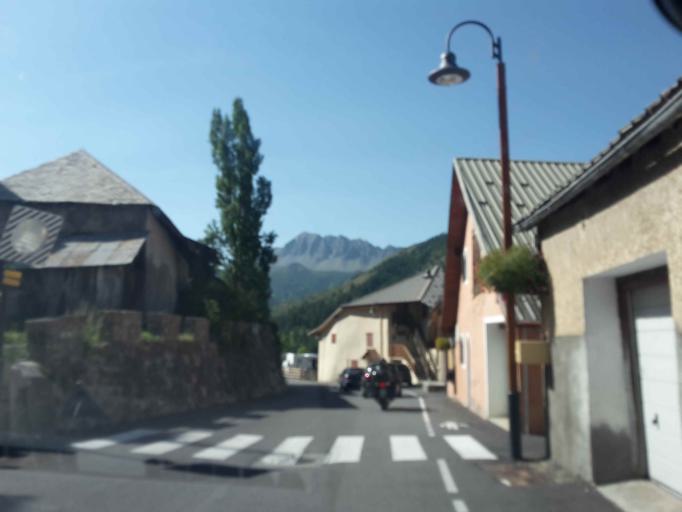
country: FR
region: Provence-Alpes-Cote d'Azur
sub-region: Departement des Hautes-Alpes
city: Guillestre
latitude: 44.6089
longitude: 6.6885
